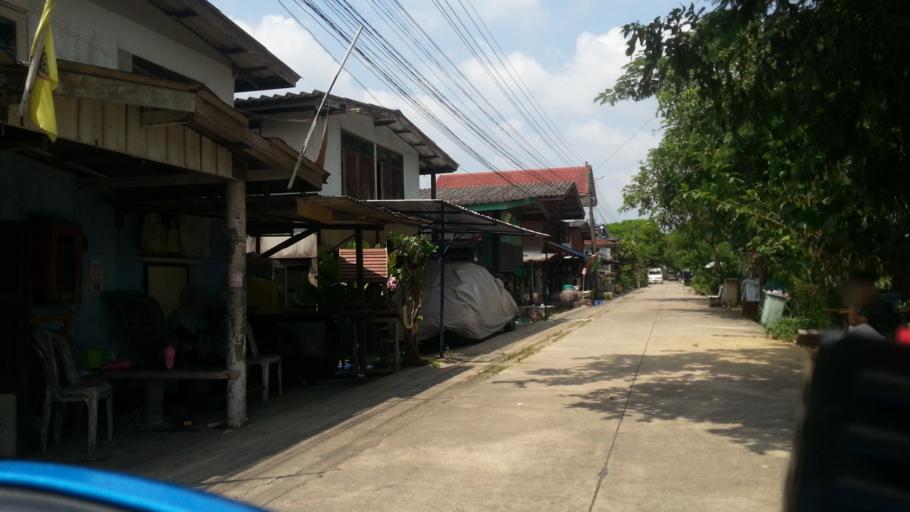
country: TH
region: Pathum Thani
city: Ban Rangsit
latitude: 14.0562
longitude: 100.8267
